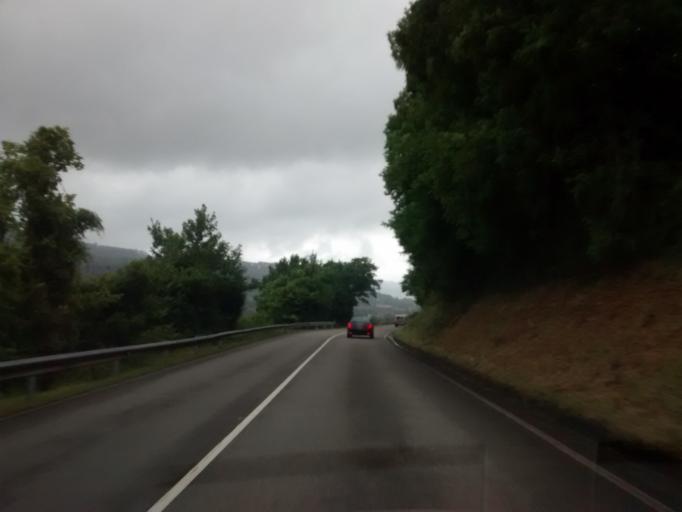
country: ES
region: Asturias
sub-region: Province of Asturias
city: Villaviciosa
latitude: 43.4990
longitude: -5.4267
